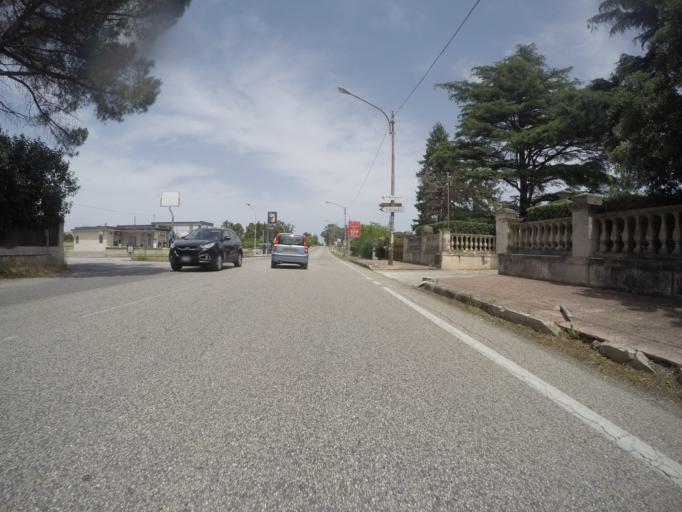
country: IT
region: Apulia
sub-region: Provincia di Taranto
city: Martina Franca
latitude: 40.6846
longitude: 17.3321
